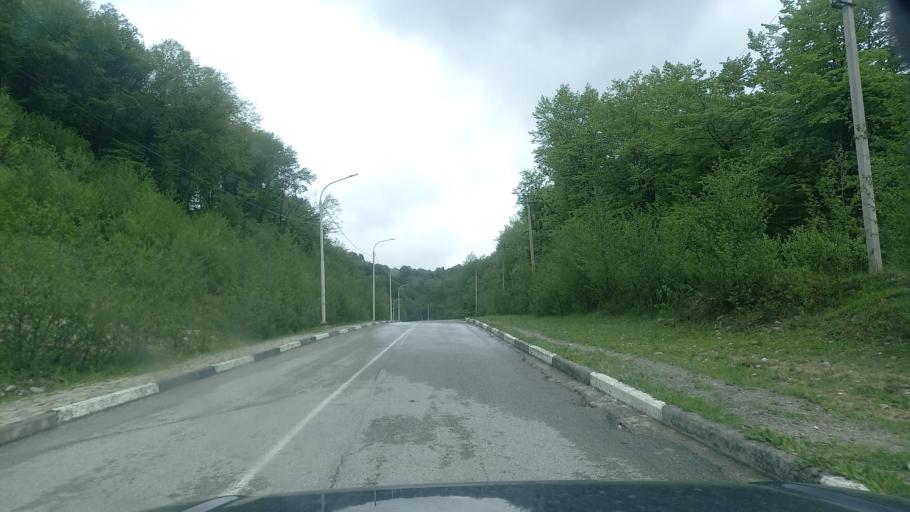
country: RU
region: Kabardino-Balkariya
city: Babugent
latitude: 43.2362
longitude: 43.5398
